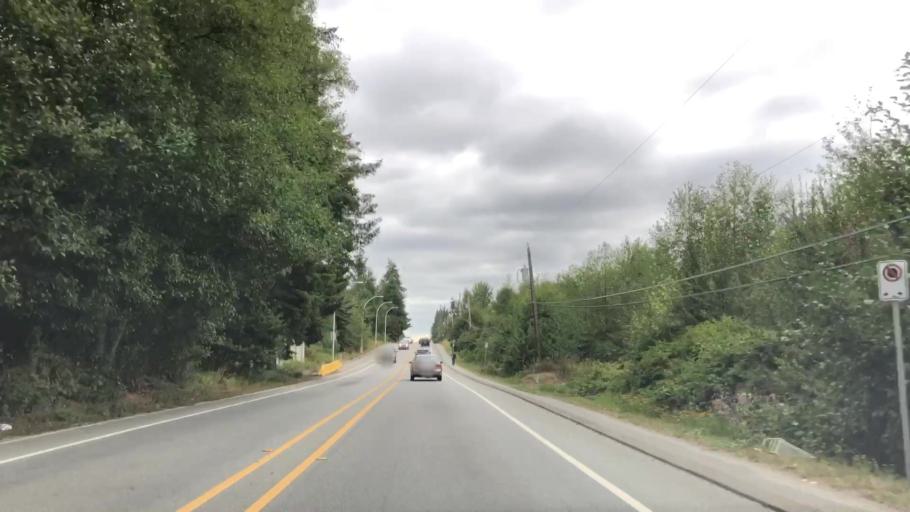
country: CA
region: British Columbia
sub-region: Greater Vancouver Regional District
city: White Rock
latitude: 49.0601
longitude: -122.7753
